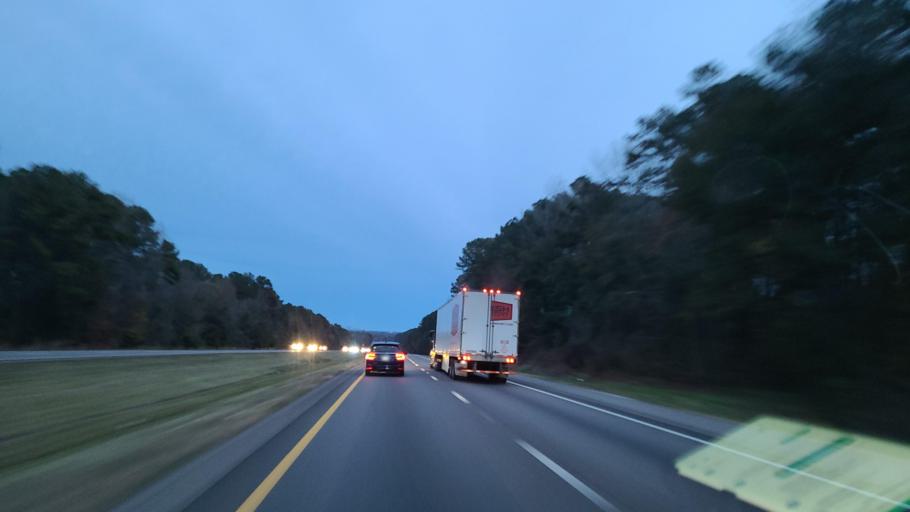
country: US
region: Mississippi
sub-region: Lauderdale County
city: Marion
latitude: 32.4056
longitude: -88.5506
